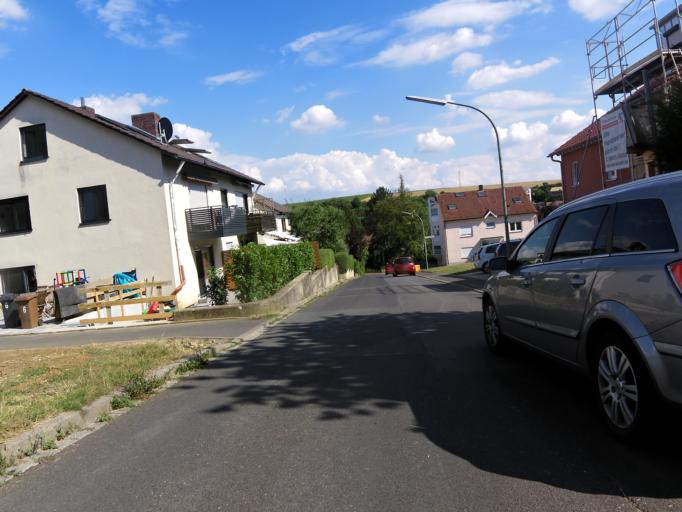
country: DE
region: Bavaria
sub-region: Regierungsbezirk Unterfranken
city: Rimpar
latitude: 49.8250
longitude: 9.9699
